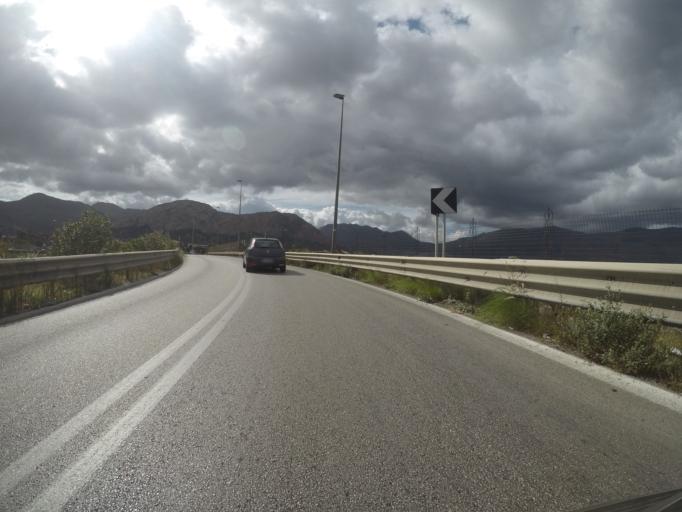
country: IT
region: Sicily
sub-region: Palermo
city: Capaci
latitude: 38.1750
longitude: 13.2150
